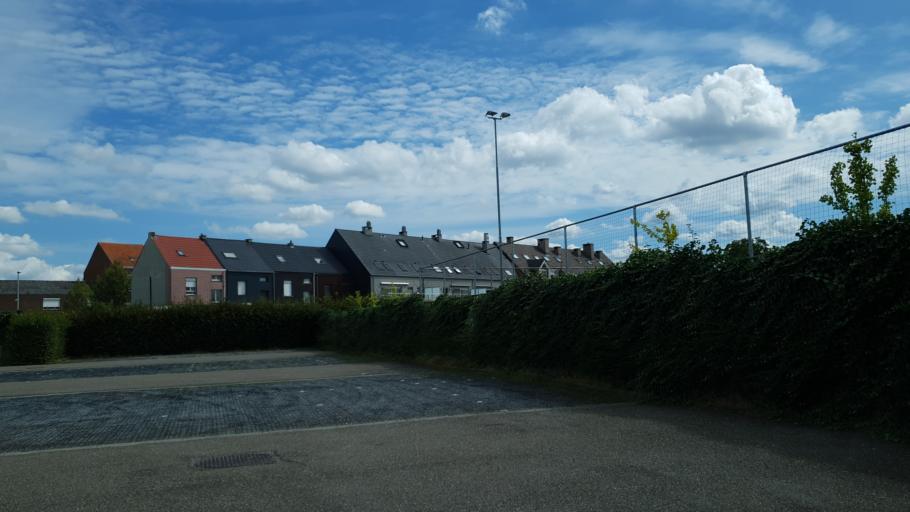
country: BE
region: Flanders
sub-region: Provincie Vlaams-Brabant
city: Herent
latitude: 50.9111
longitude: 4.6609
